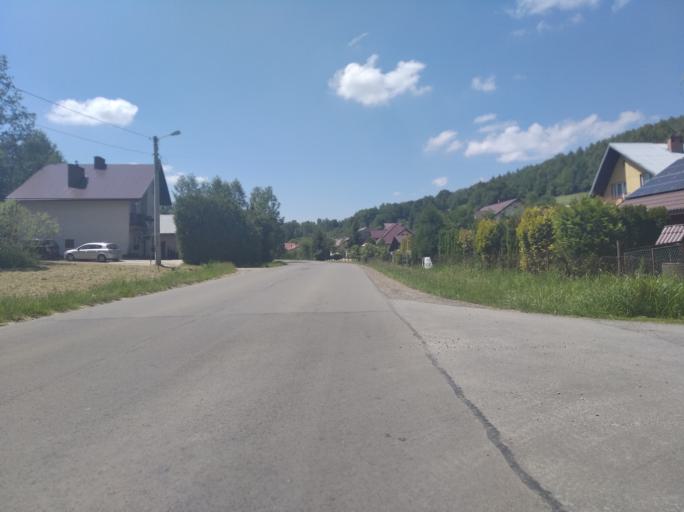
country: PL
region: Subcarpathian Voivodeship
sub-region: Powiat brzozowski
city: Jablonka
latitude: 49.6987
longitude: 22.1208
